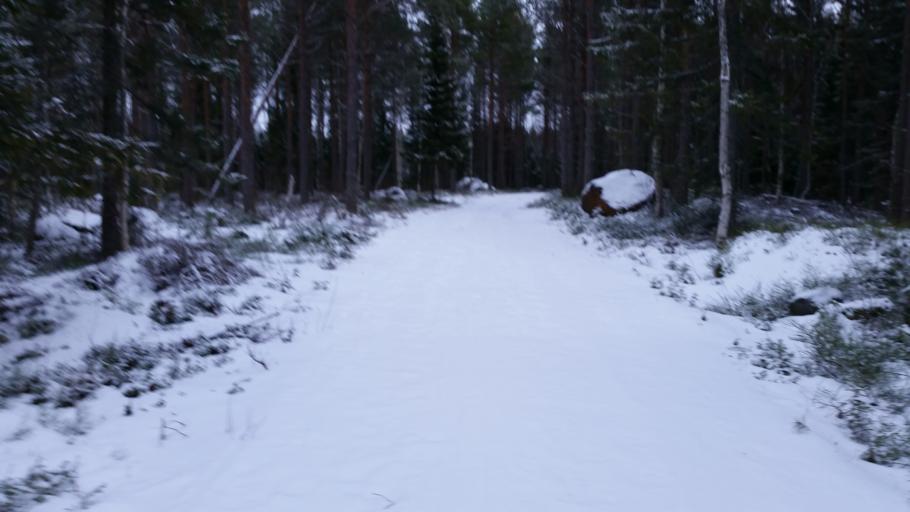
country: SE
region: Vaesterbotten
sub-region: Umea Kommun
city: Saevar
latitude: 63.9153
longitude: 20.7892
